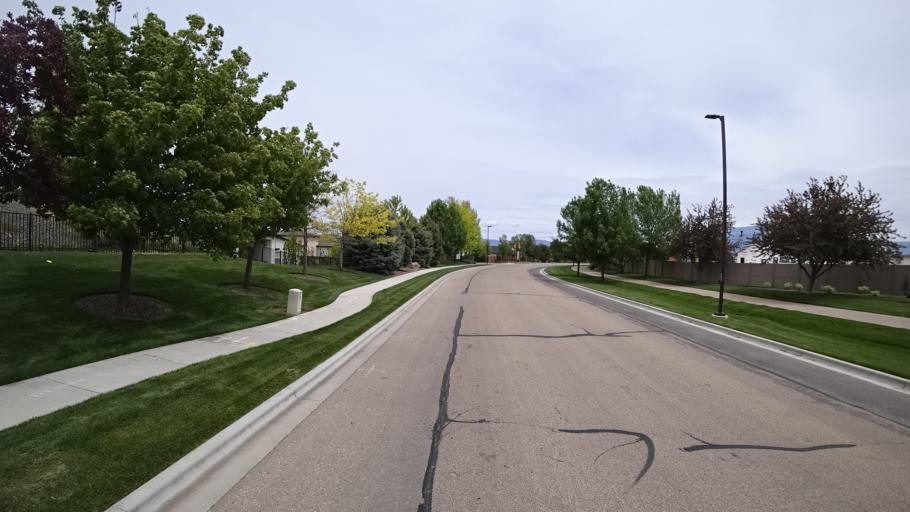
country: US
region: Idaho
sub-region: Ada County
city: Meridian
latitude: 43.5531
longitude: -116.3630
